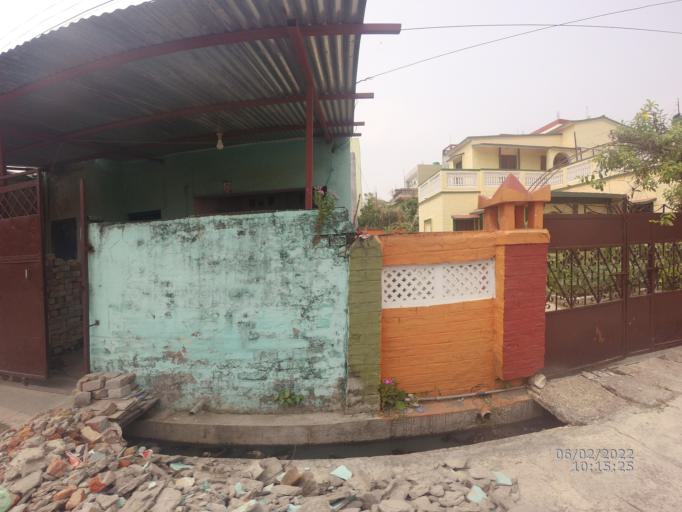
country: NP
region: Western Region
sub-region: Lumbini Zone
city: Bhairahawa
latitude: 27.5109
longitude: 83.4526
